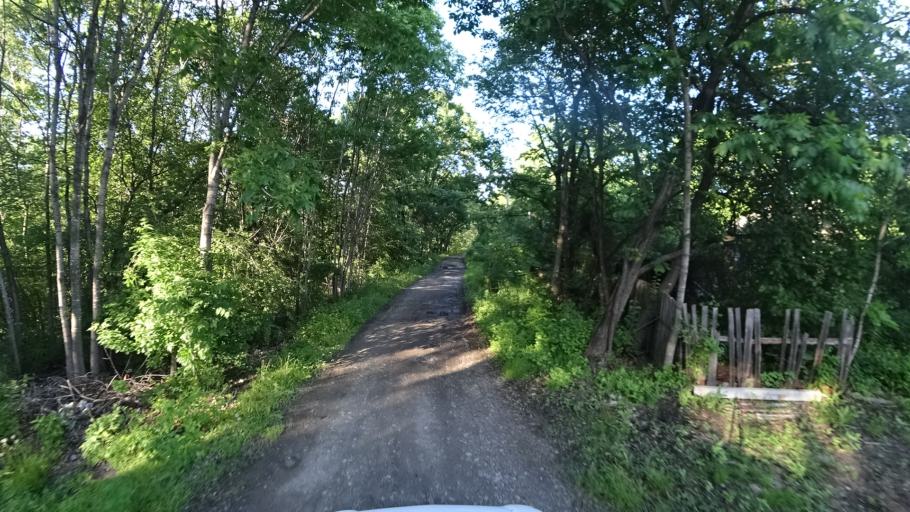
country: RU
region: Khabarovsk Krai
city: Khor
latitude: 47.8503
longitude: 134.9437
